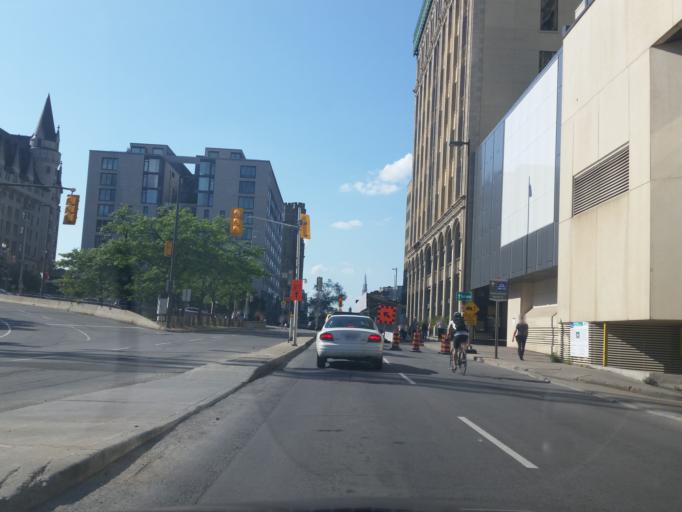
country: CA
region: Ontario
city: Ottawa
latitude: 45.4247
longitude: -75.6927
